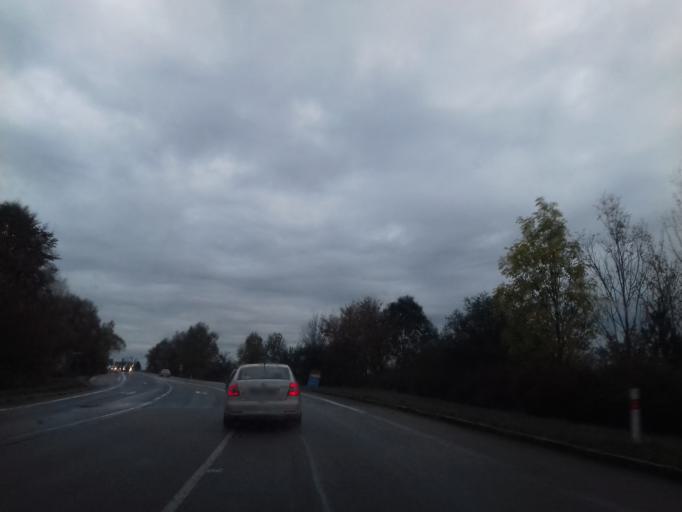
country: CZ
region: Pardubicky
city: Horni Jeleni
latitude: 50.0022
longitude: 16.1010
